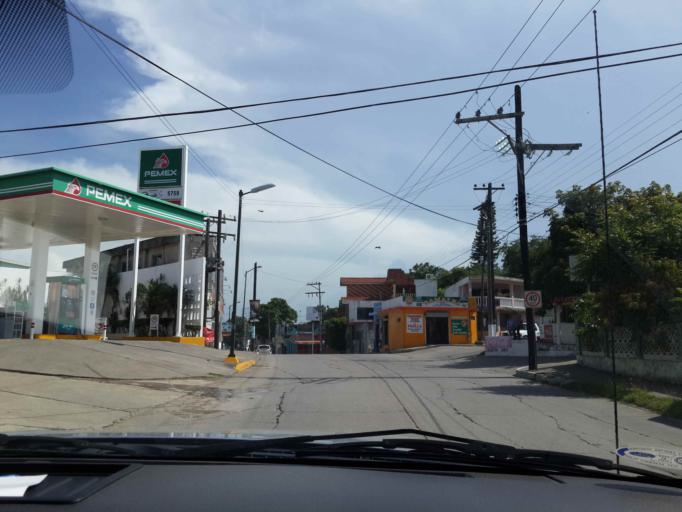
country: MX
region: Tamaulipas
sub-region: Tampico
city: Tampico
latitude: 22.2510
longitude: -97.8668
